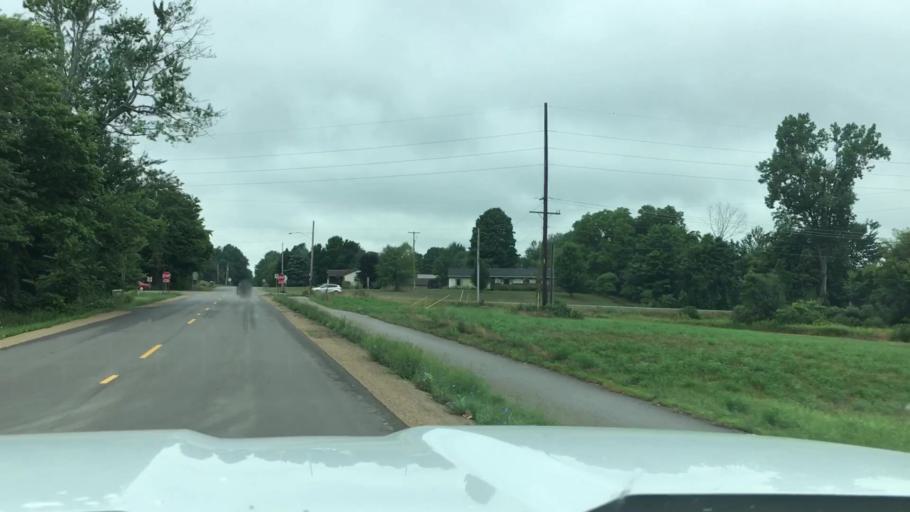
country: US
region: Michigan
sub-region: Ottawa County
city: Jenison
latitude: 42.8406
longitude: -85.8007
